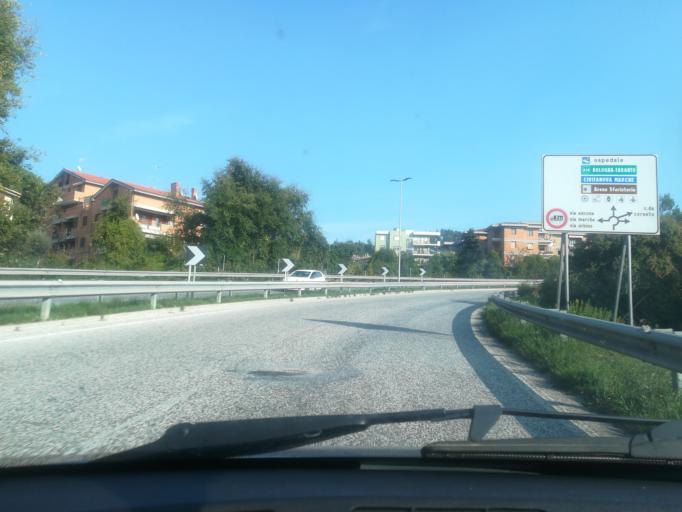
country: IT
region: The Marches
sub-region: Provincia di Macerata
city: Macerata
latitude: 43.2917
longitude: 13.4546
